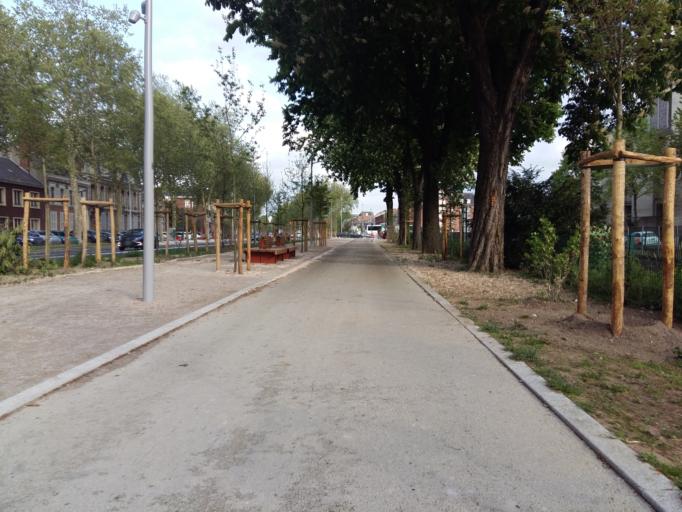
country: FR
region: Picardie
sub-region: Departement de la Somme
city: Amiens
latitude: 49.8911
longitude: 2.2892
